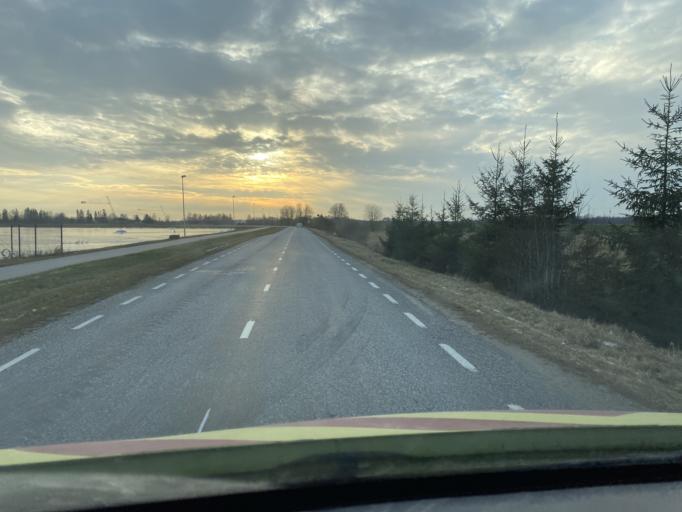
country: EE
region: Jogevamaa
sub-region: Poltsamaa linn
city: Poltsamaa
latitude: 58.6207
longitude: 25.9827
